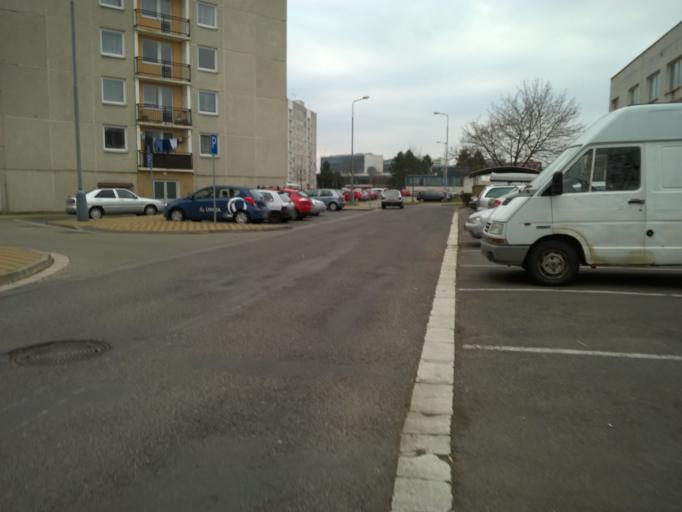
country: CZ
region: Pardubicky
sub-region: Okres Pardubice
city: Pardubice
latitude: 50.0526
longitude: 15.7697
